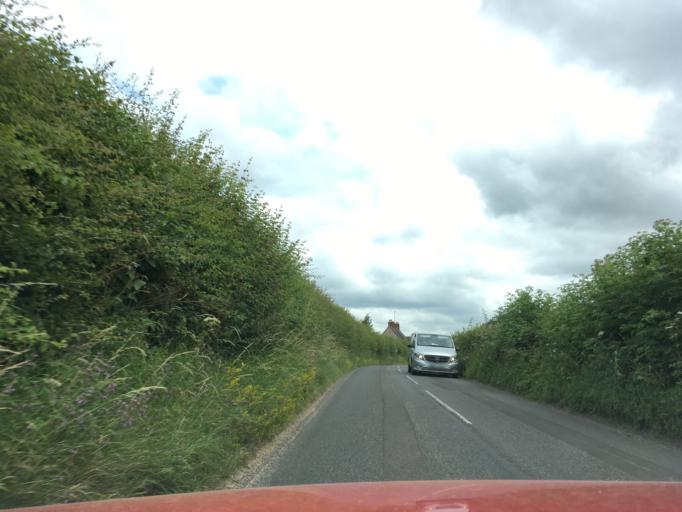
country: GB
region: England
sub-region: Oxfordshire
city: Shipton under Wychwood
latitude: 51.8763
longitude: -1.6641
